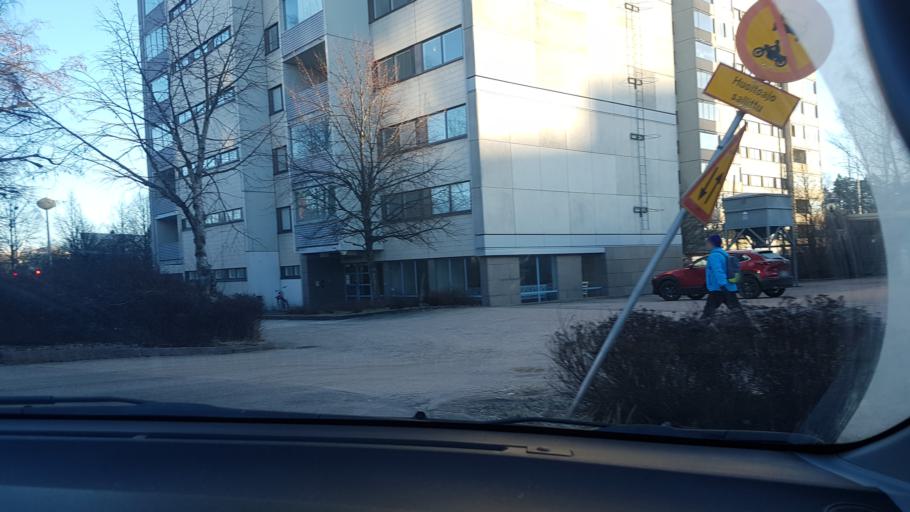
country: FI
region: Uusimaa
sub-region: Helsinki
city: Kerava
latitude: 60.4043
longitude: 25.0984
